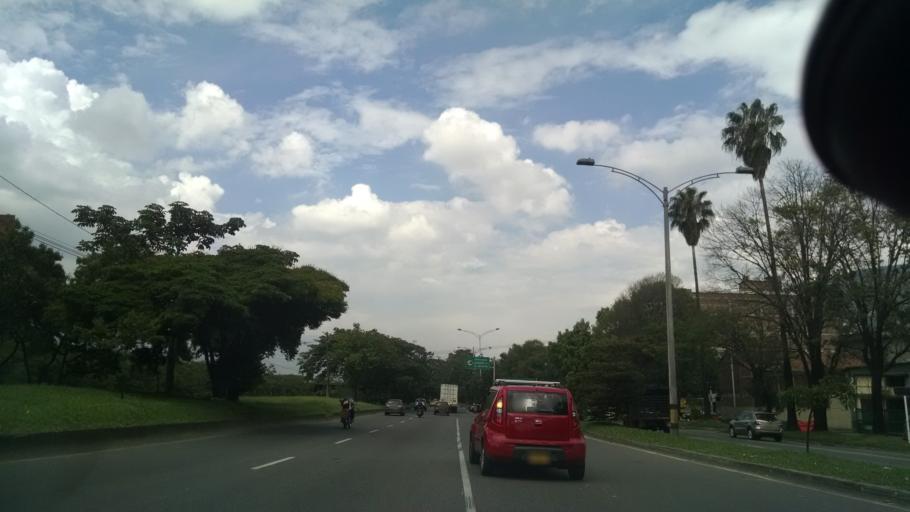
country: CO
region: Antioquia
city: Medellin
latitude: 6.2516
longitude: -75.5782
